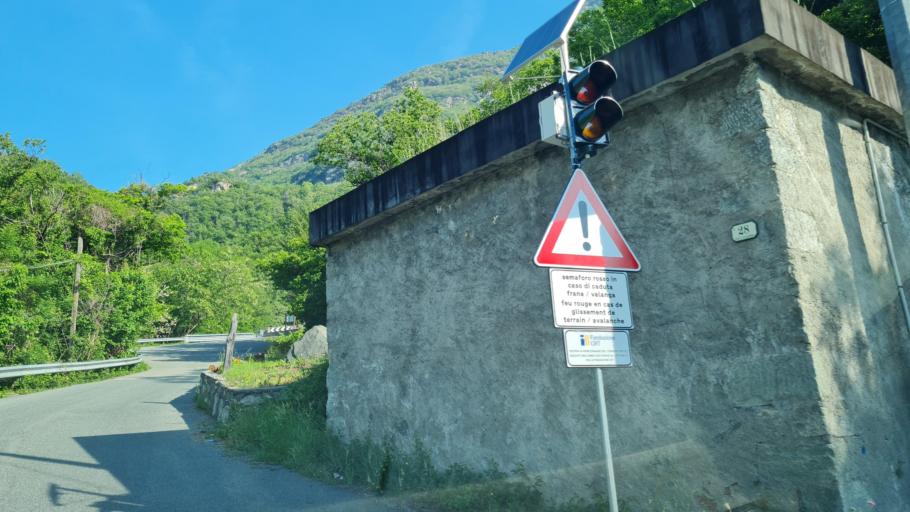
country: IT
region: Aosta Valley
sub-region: Valle d'Aosta
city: Donnas
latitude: 45.6085
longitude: 7.7680
